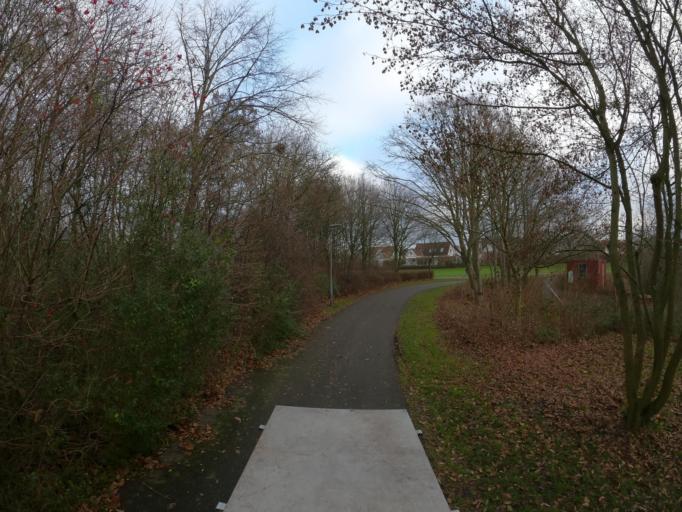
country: SE
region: Skane
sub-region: Svedala Kommun
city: Svedala
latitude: 55.5194
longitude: 13.2165
